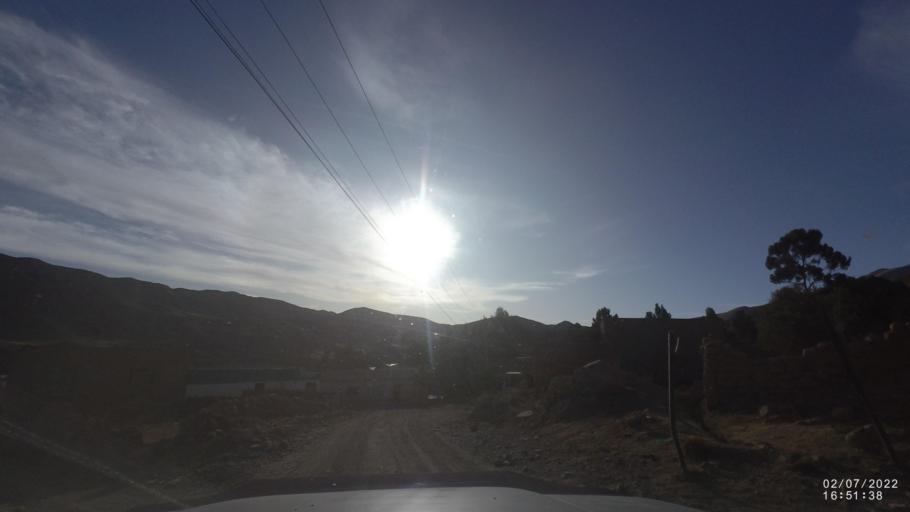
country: BO
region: Cochabamba
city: Irpa Irpa
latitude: -17.9695
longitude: -66.5349
